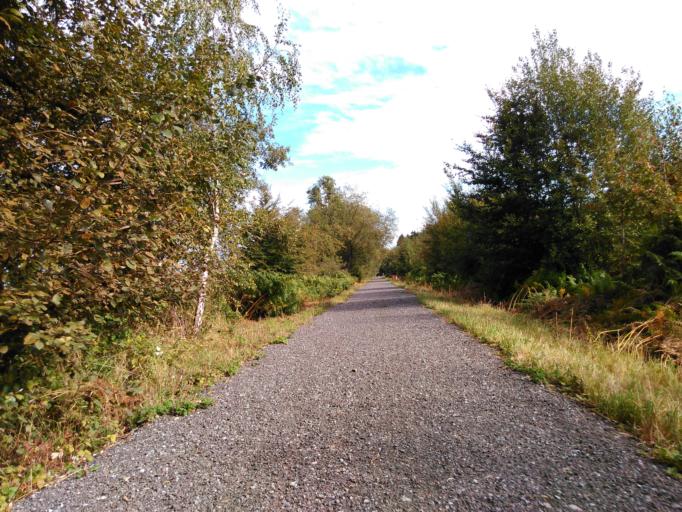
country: BE
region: Wallonia
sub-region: Province du Luxembourg
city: Vaux-sur-Sure
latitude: 49.9263
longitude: 5.5115
